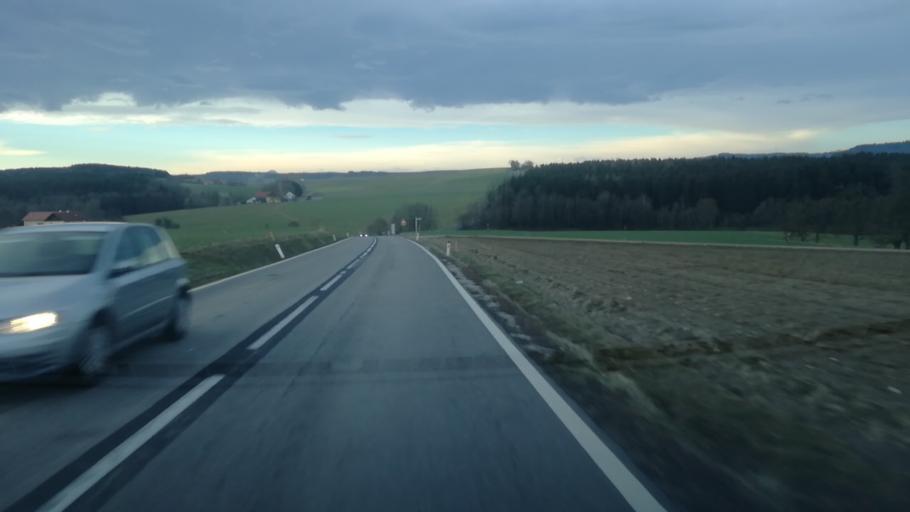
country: AT
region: Upper Austria
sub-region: Politischer Bezirk Ried im Innkreis
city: Waldzell
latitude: 48.1719
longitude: 13.4435
